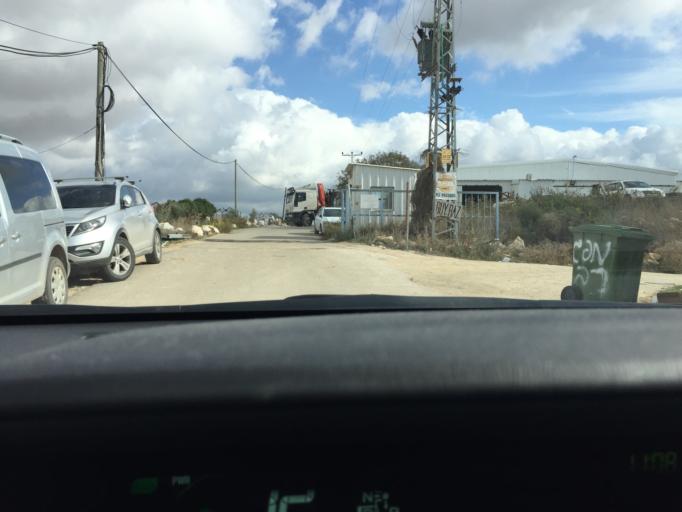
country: PS
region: West Bank
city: Kafr ad Dik
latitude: 32.0696
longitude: 35.0676
